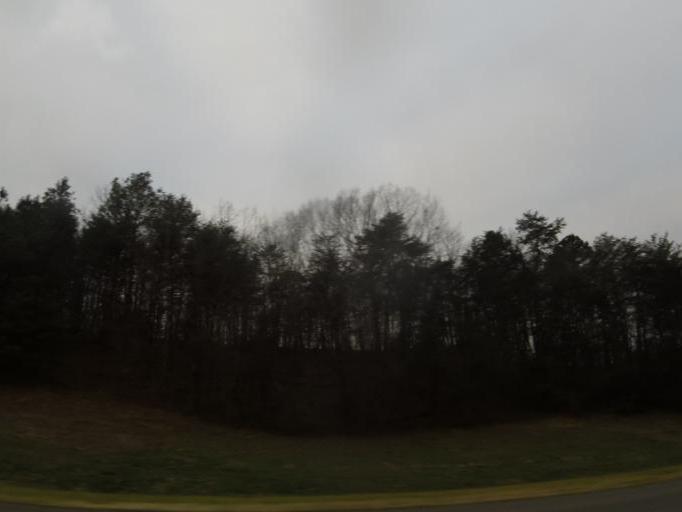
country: US
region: Alabama
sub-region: Jefferson County
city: Morris
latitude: 33.7432
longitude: -86.8271
